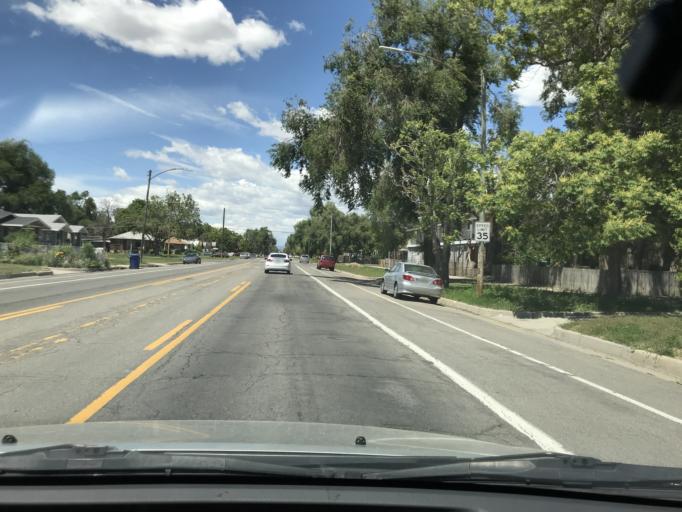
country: US
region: Utah
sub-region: Salt Lake County
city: Salt Lake City
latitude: 40.7771
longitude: -111.9168
